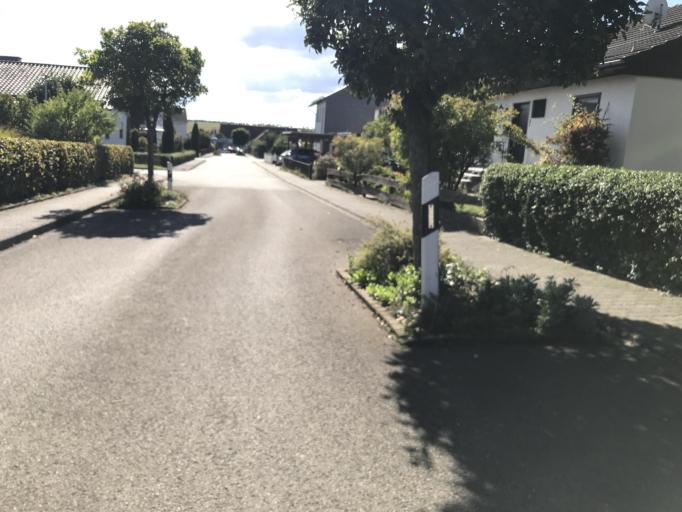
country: DE
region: Hesse
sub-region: Regierungsbezirk Kassel
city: Sachsenhausen
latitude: 51.2739
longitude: 8.9826
